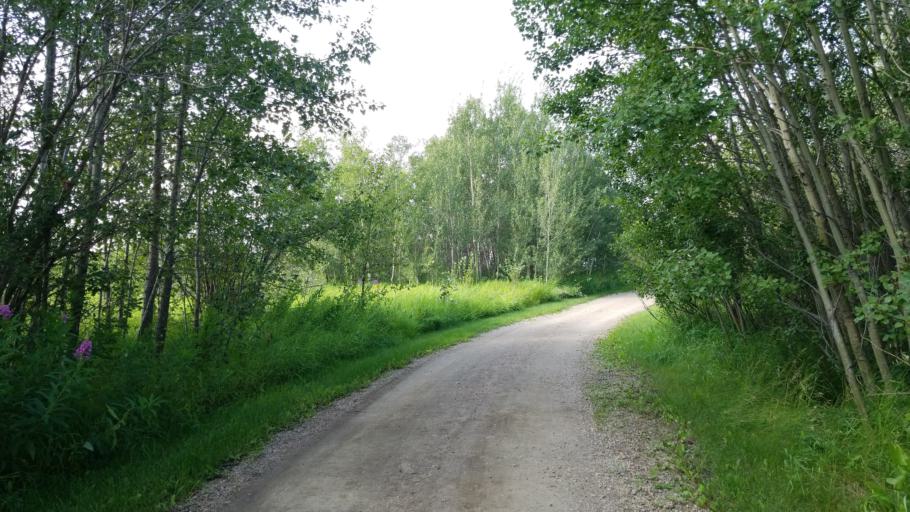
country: CA
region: Saskatchewan
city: Lloydminster
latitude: 53.2598
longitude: -110.0478
